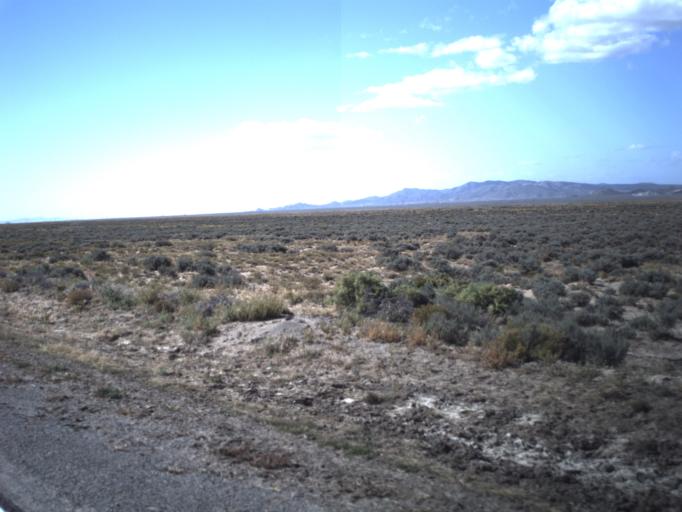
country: US
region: Utah
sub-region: Beaver County
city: Milford
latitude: 38.4796
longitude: -112.9911
